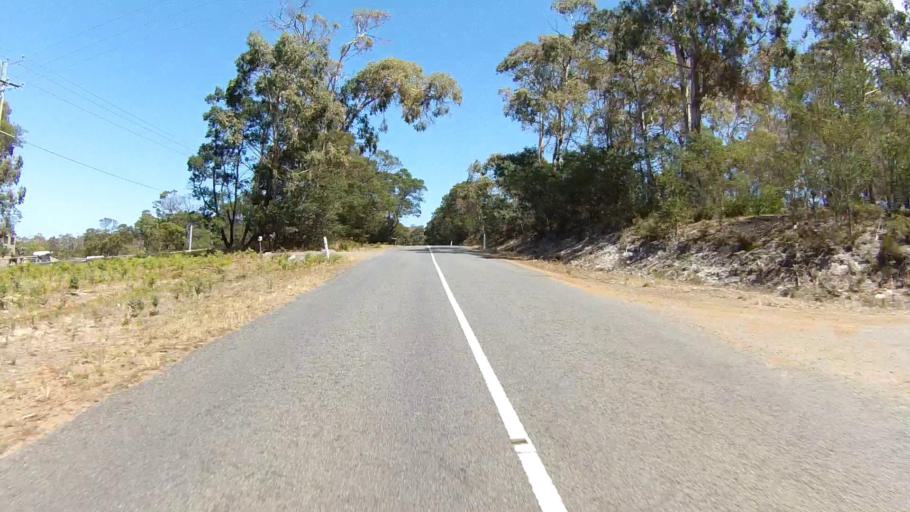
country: AU
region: Tasmania
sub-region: Clarence
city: Sandford
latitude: -42.9916
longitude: 147.4782
